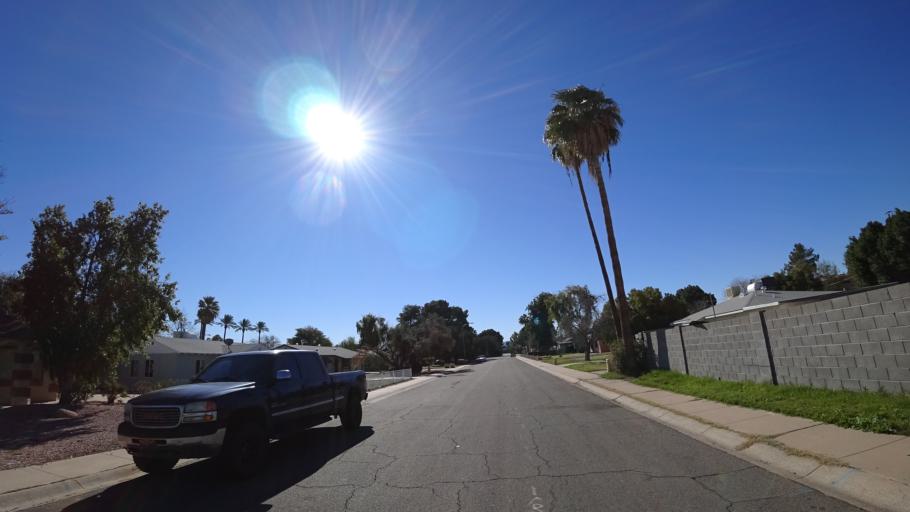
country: US
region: Arizona
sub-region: Maricopa County
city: Phoenix
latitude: 33.5051
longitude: -112.0585
